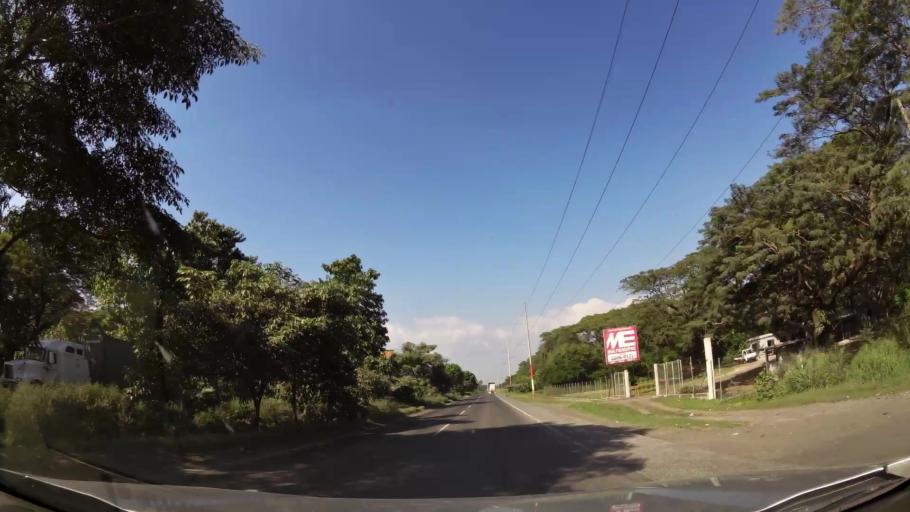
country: GT
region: Escuintla
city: Puerto San Jose
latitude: 13.9455
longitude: -90.7884
